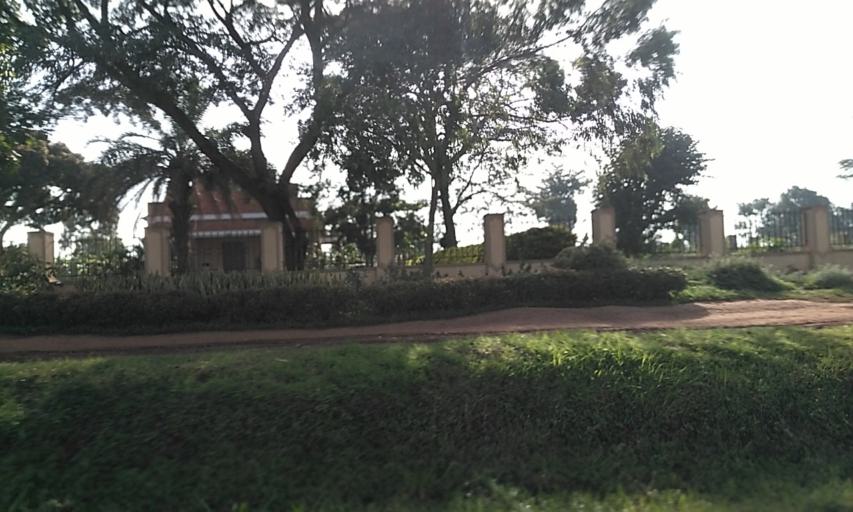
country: UG
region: Central Region
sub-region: Wakiso District
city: Kireka
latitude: 0.4237
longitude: 32.5983
